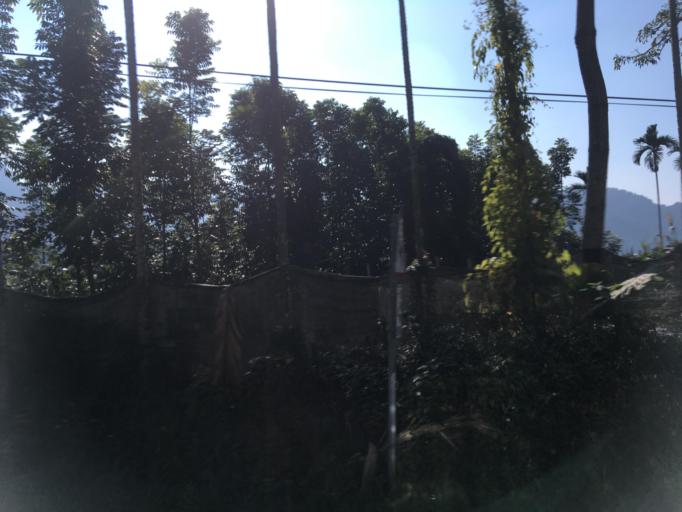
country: TW
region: Taiwan
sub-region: Chiayi
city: Jiayi Shi
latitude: 23.4341
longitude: 120.6307
